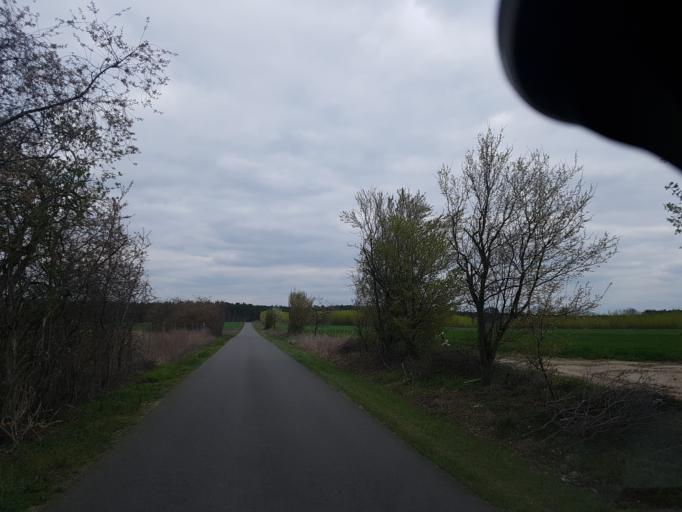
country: DE
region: Brandenburg
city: Linthe
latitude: 52.1199
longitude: 12.8000
